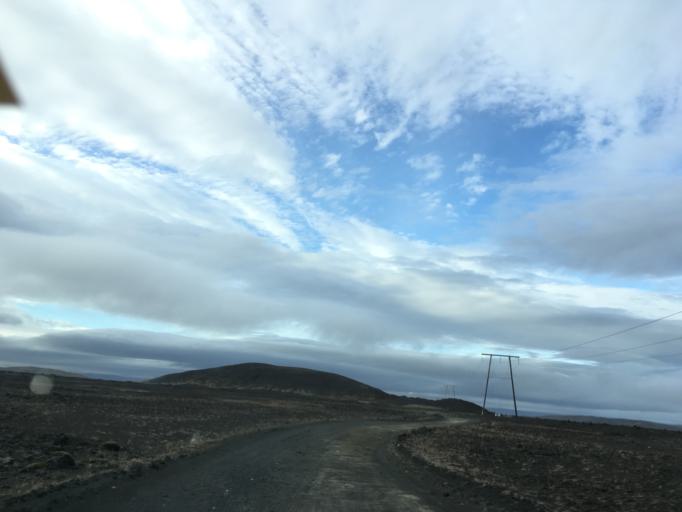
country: IS
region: South
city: Vestmannaeyjar
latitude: 64.1216
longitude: -19.1178
